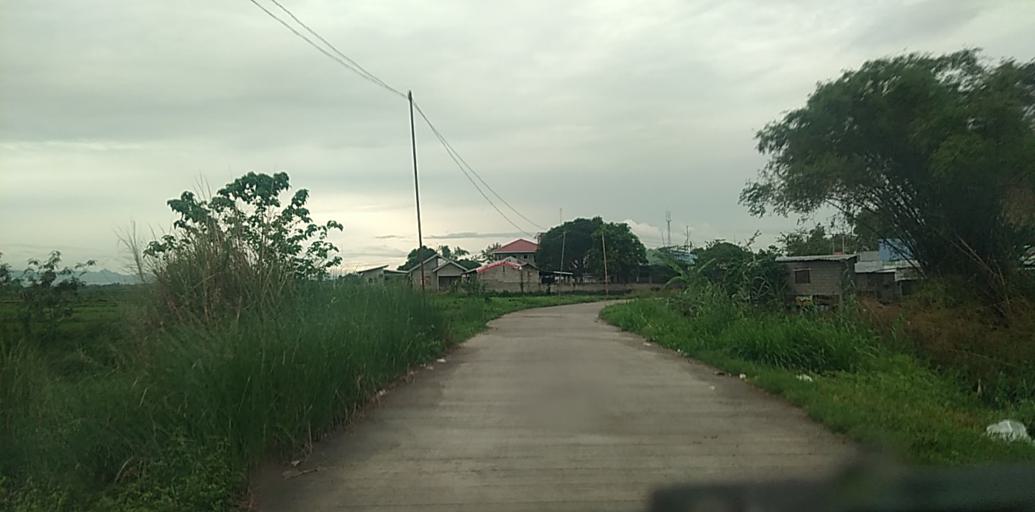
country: PH
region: Central Luzon
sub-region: Province of Pampanga
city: Anao
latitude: 15.1442
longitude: 120.7257
